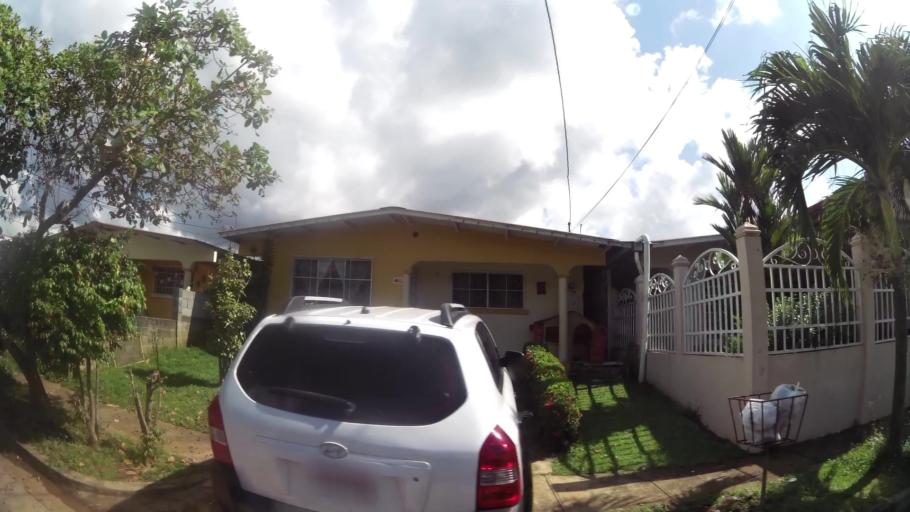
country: PA
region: Panama
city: Nuevo Arraijan
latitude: 8.9100
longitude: -79.7397
